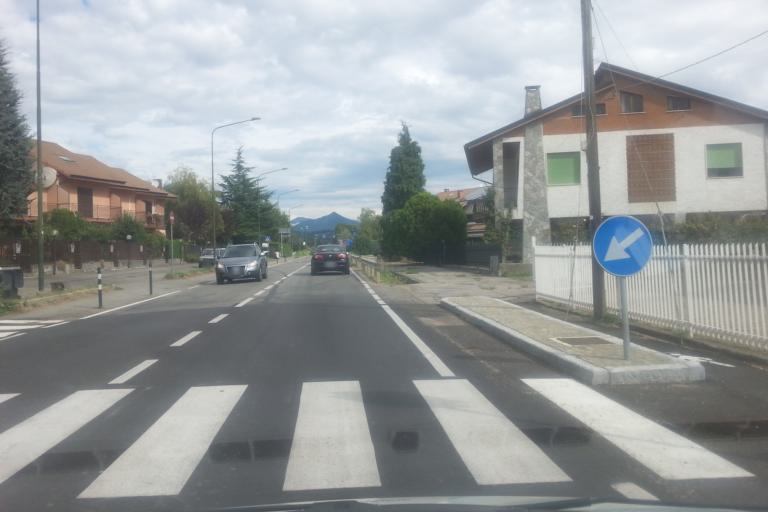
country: IT
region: Piedmont
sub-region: Provincia di Torino
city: Piossasco
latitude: 44.9996
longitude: 7.4672
